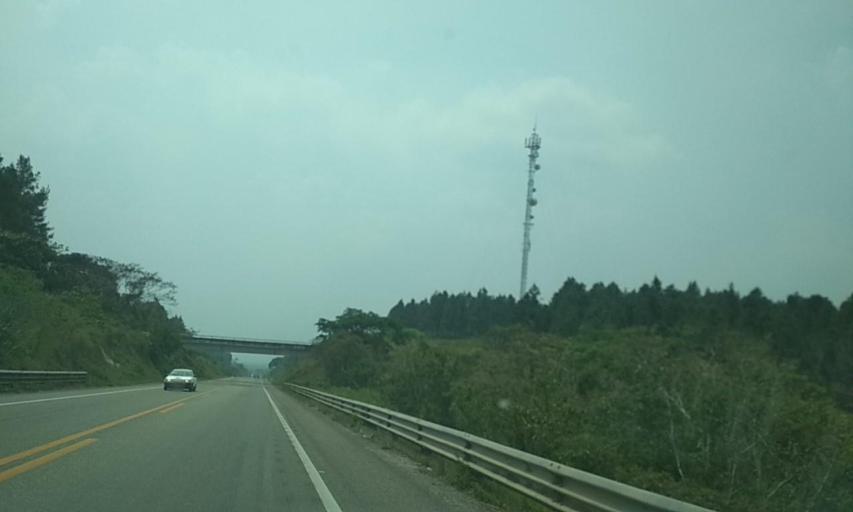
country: MX
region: Tabasco
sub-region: Huimanguillo
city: Francisco Rueda
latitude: 17.7491
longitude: -93.9931
